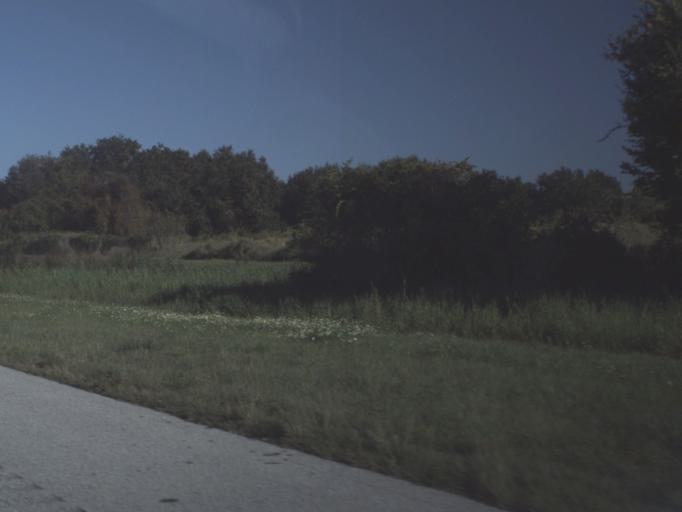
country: US
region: Florida
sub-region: Lake County
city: Hawthorne
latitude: 28.6974
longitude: -81.8775
